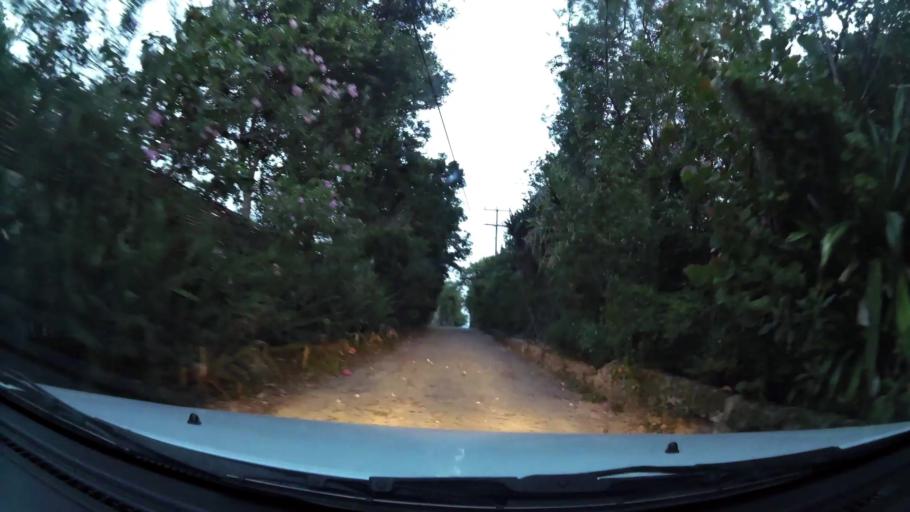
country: BB
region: Saint Philip
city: Crane
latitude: 13.1085
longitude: -59.4436
